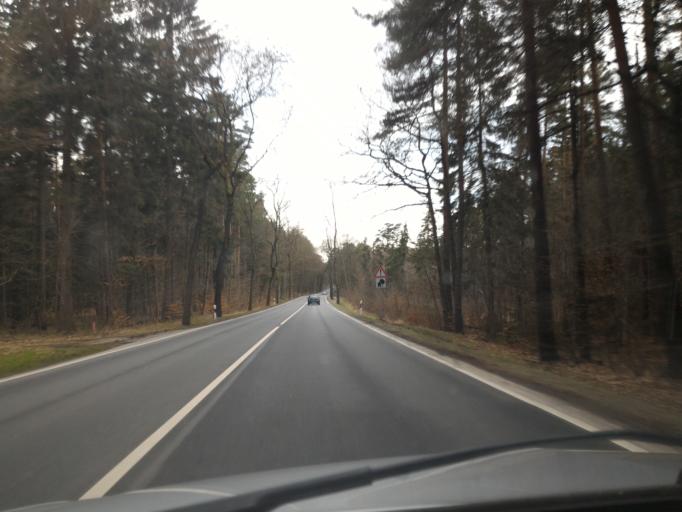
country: DE
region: Saxony
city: Arnsdorf
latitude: 51.0643
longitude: 13.9694
